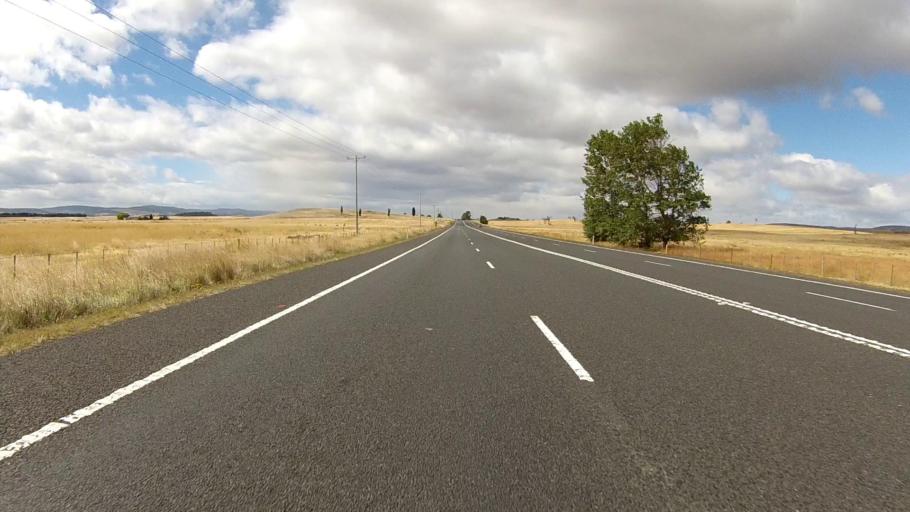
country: AU
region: Tasmania
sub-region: Northern Midlands
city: Evandale
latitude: -41.8730
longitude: 147.4604
